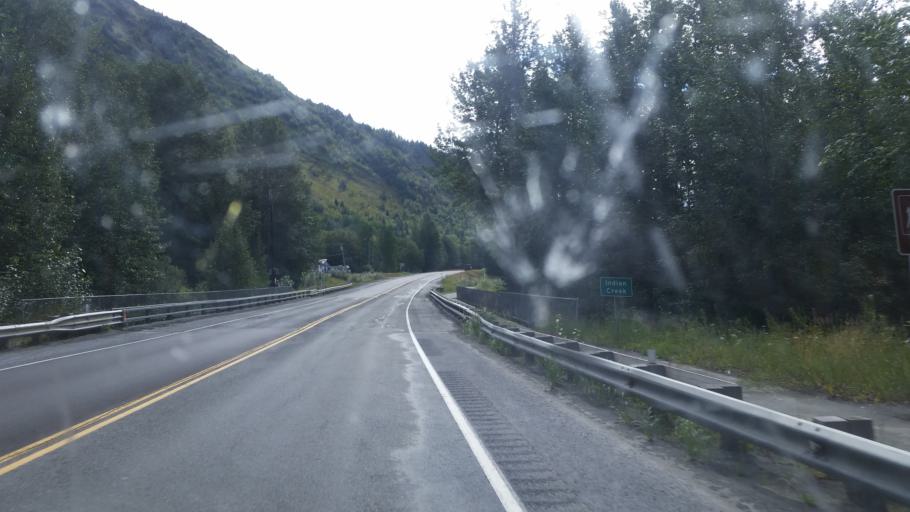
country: US
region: Alaska
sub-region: Anchorage Municipality
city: Elmendorf Air Force Base
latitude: 60.9857
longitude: -149.5015
